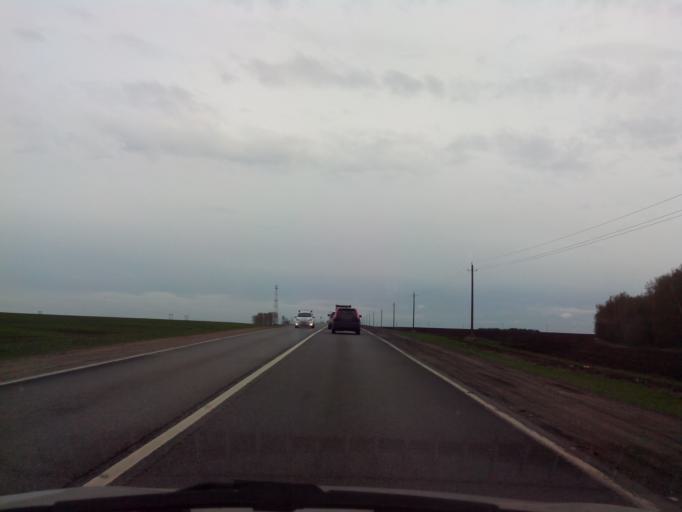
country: RU
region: Moskovskaya
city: Ozherel'ye
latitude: 54.7080
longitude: 38.2955
